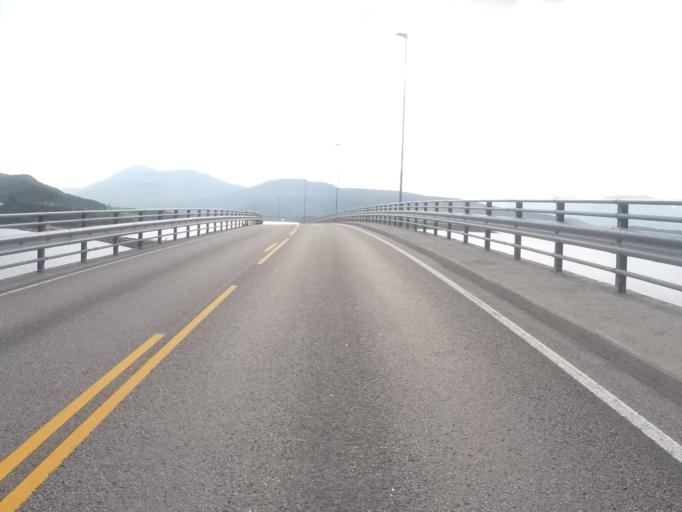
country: NO
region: More og Romsdal
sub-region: Molde
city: Hjelset
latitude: 62.7308
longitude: 7.3544
